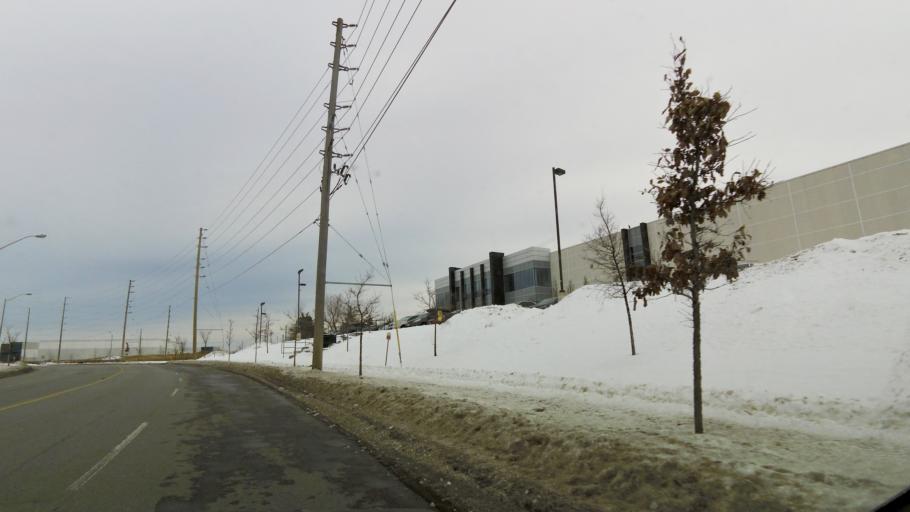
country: CA
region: Ontario
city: Etobicoke
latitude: 43.7817
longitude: -79.6498
